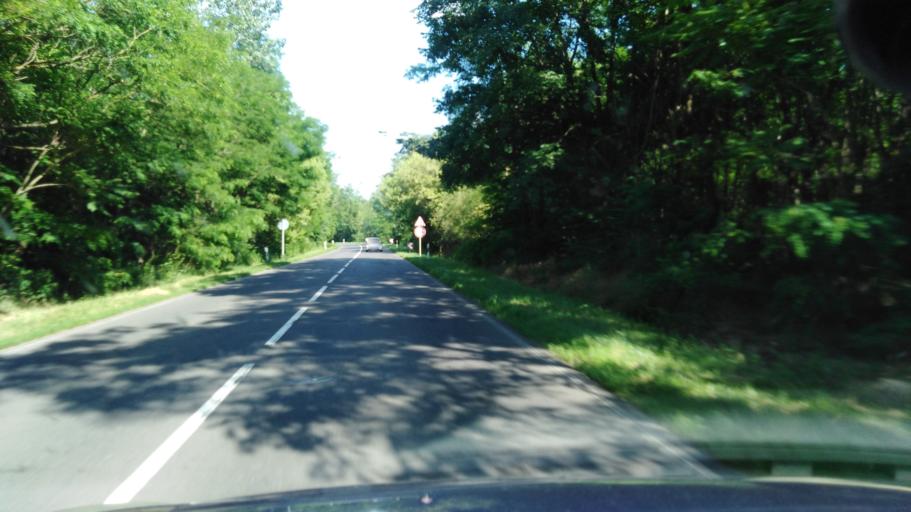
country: HU
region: Szabolcs-Szatmar-Bereg
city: Nyirvasvari
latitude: 47.8113
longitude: 22.2247
